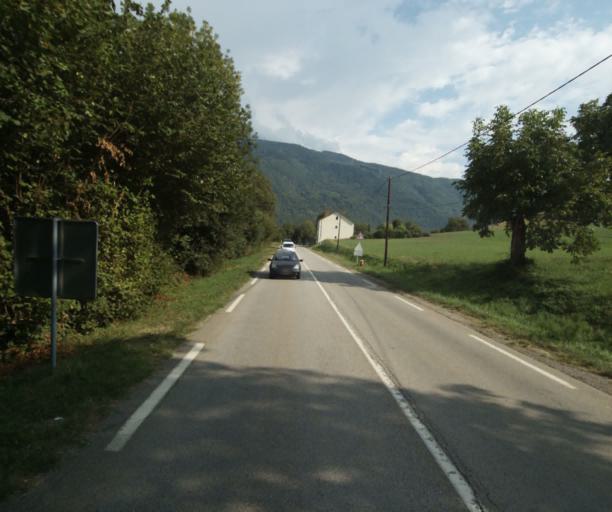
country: FR
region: Rhone-Alpes
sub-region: Departement de l'Isere
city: Brie-et-Angonnes
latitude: 45.1089
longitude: 5.7895
